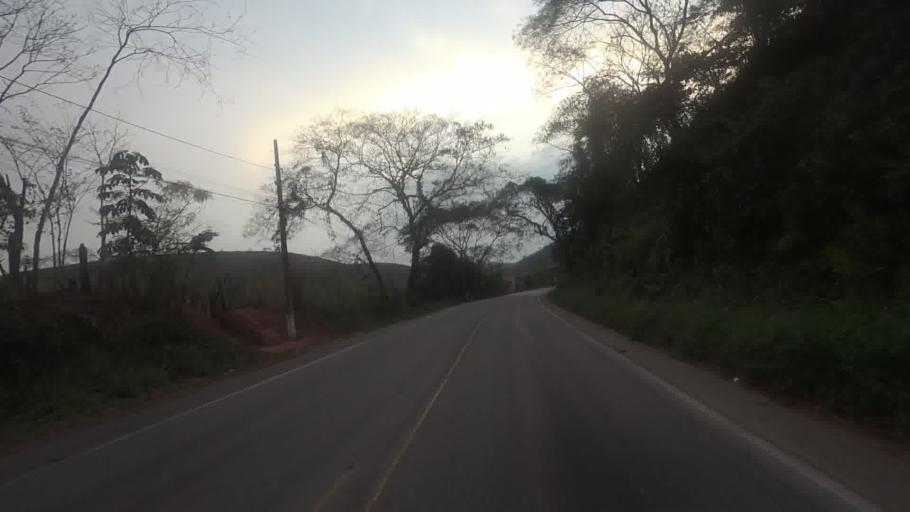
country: BR
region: Rio de Janeiro
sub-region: Carmo
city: Carmo
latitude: -21.8384
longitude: -42.6135
